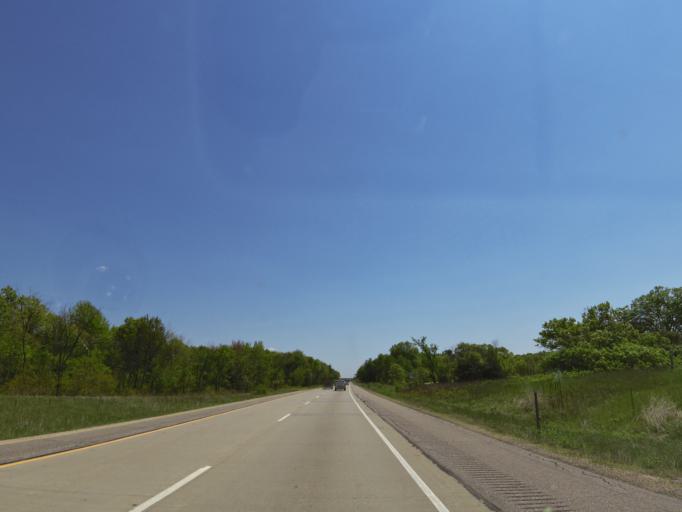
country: US
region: Wisconsin
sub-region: Juneau County
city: New Lisbon
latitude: 43.8697
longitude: -90.1246
